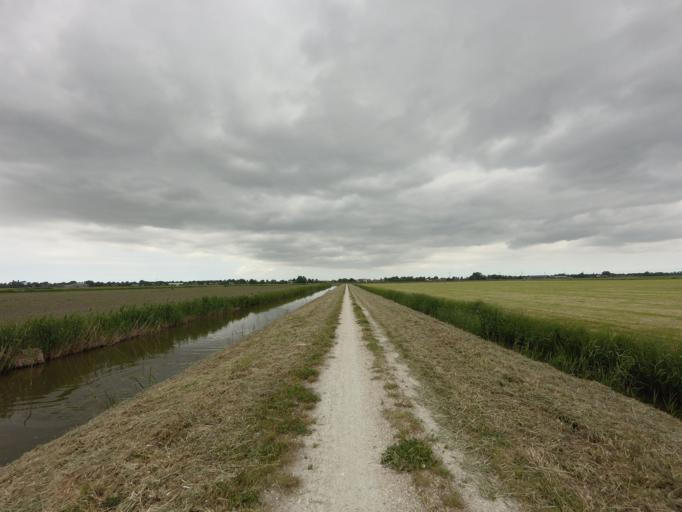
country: NL
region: North Holland
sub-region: Gemeente Hoorn
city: Hoorn
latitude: 52.6087
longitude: 4.9729
